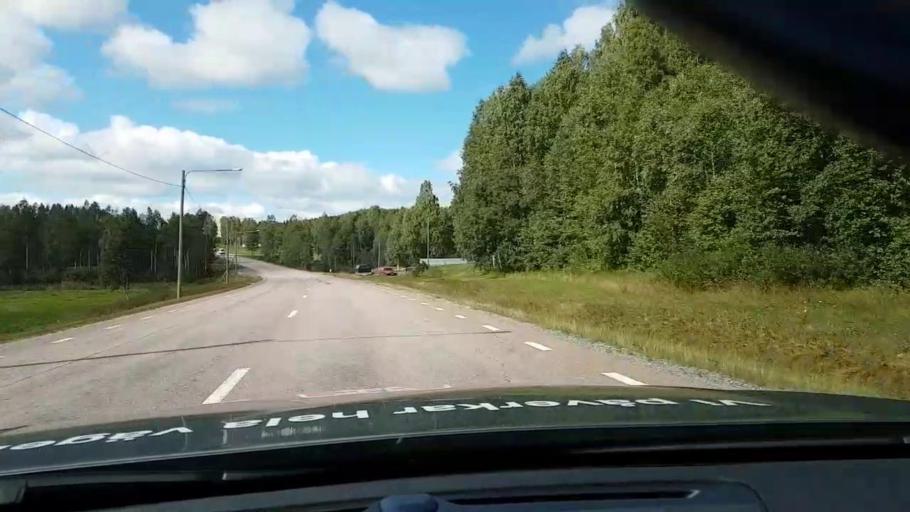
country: SE
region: Vaesternorrland
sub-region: OErnskoeldsviks Kommun
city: Bjasta
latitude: 63.3881
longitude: 18.3660
